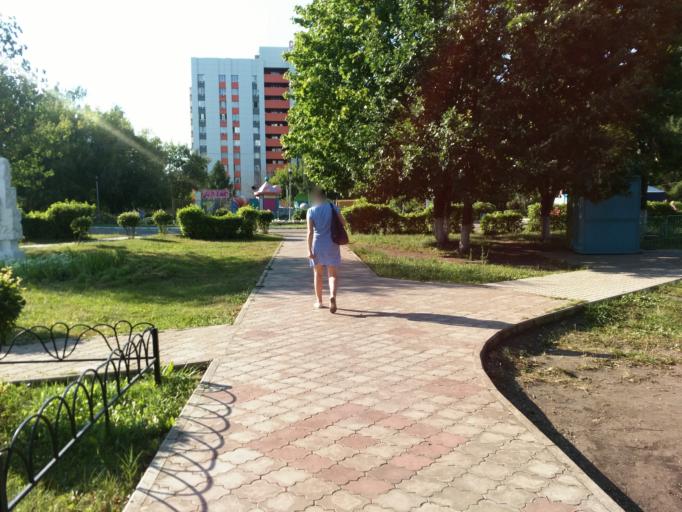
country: RU
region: Tatarstan
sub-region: Tukayevskiy Rayon
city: Naberezhnyye Chelny
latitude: 55.7553
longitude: 52.4247
